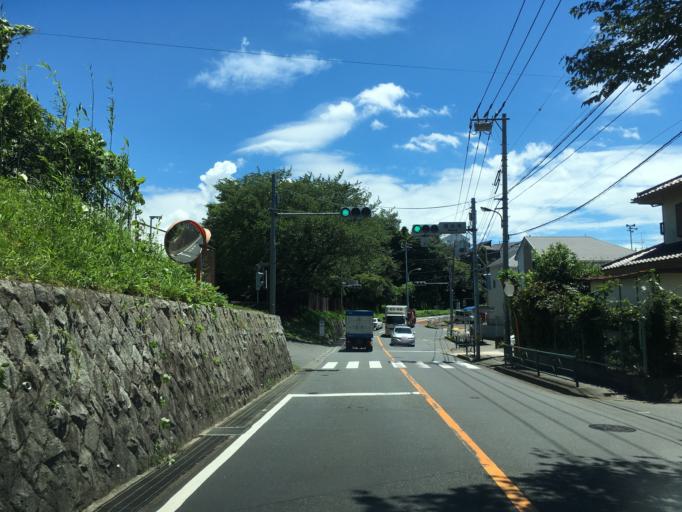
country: JP
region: Tokyo
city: Kokubunji
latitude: 35.6354
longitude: 139.4643
